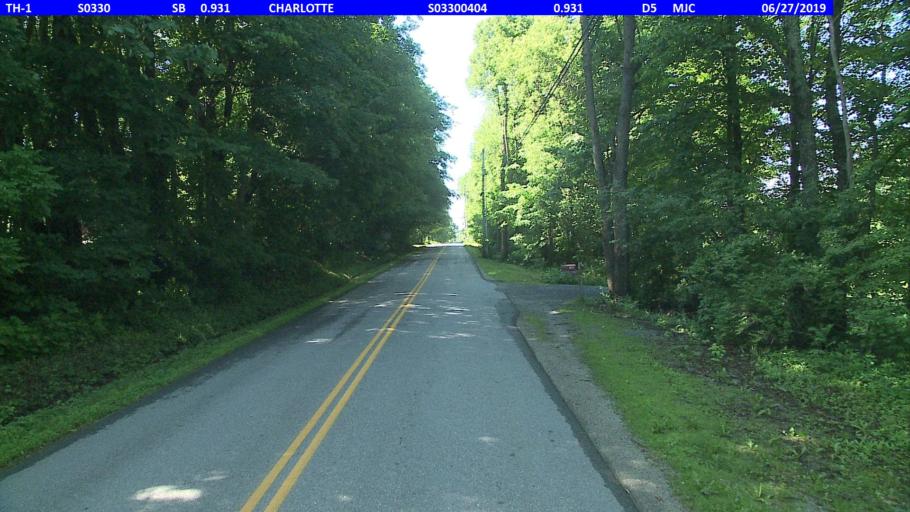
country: US
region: Vermont
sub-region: Chittenden County
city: Hinesburg
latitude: 44.3328
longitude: -73.1922
